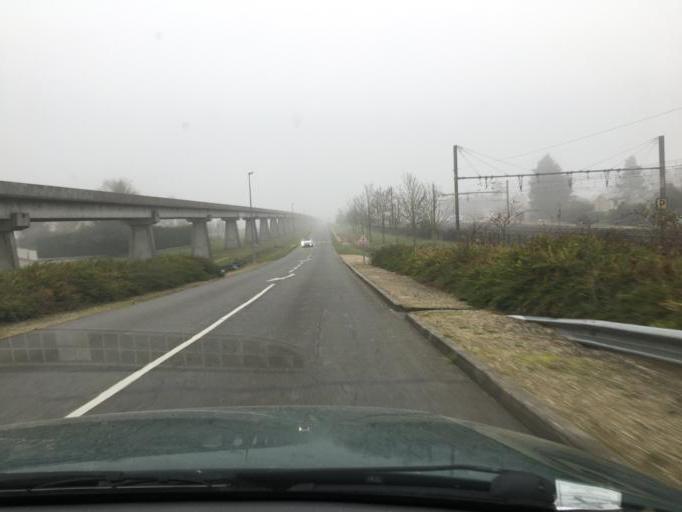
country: FR
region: Centre
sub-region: Departement du Loiret
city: Saran
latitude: 47.9890
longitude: 1.8846
